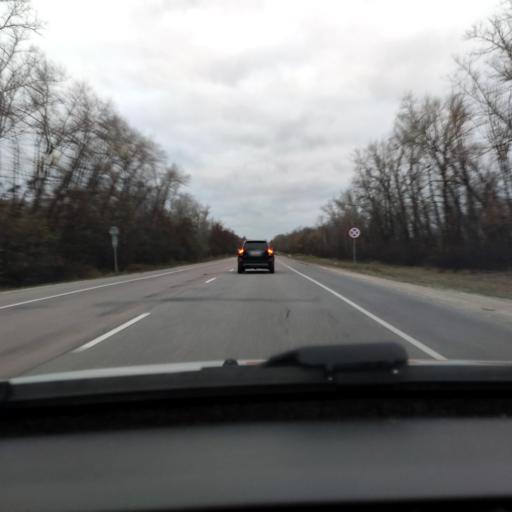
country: RU
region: Lipetsk
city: Khlevnoye
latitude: 52.2725
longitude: 39.1684
